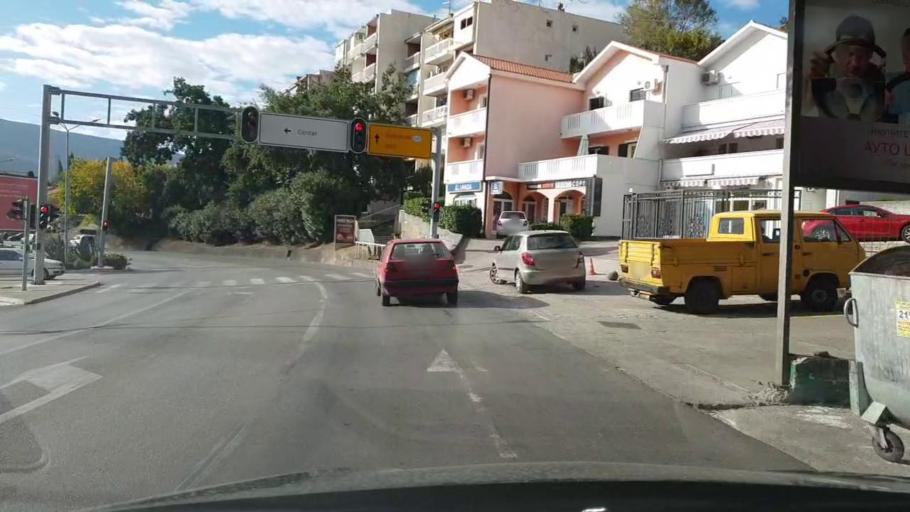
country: ME
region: Herceg Novi
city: Herceg-Novi
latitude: 42.4588
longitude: 18.5264
